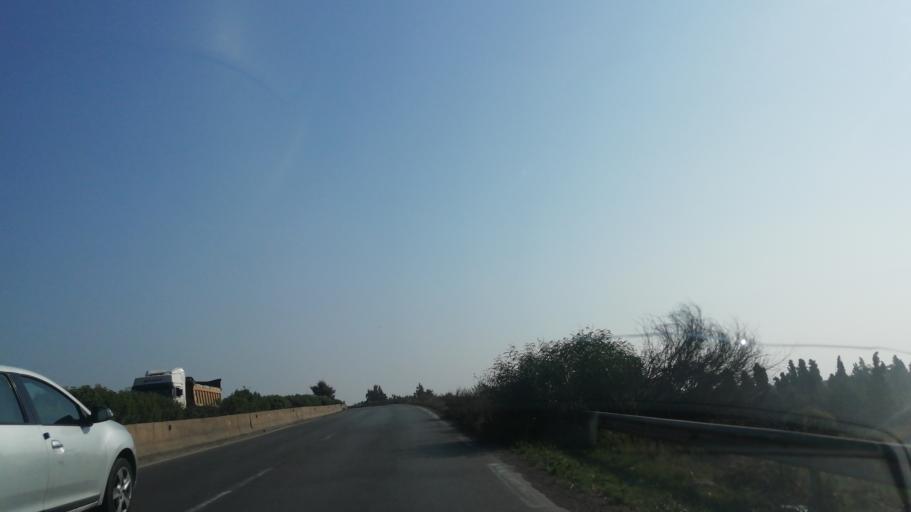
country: DZ
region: Oran
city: Bou Tlelis
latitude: 35.5668
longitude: -0.9068
